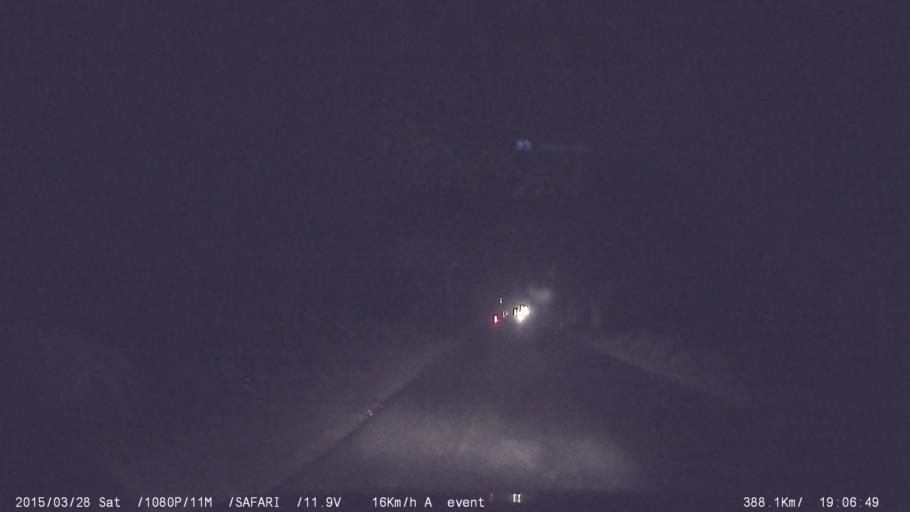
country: IN
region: Karnataka
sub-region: Mandya
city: Shrirangapattana
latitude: 12.3932
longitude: 76.6111
